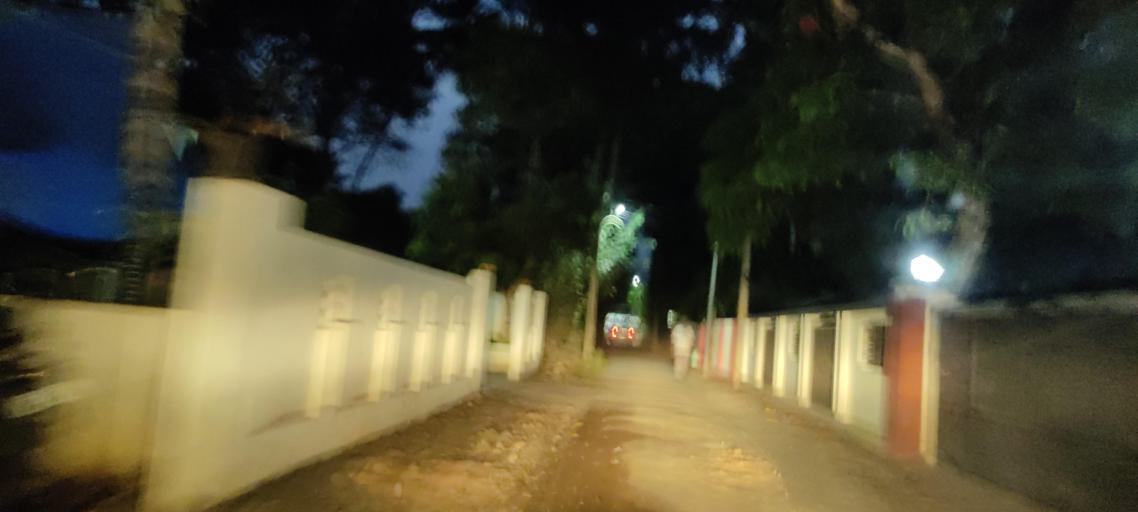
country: IN
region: Kerala
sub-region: Alappuzha
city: Mavelikara
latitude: 9.3195
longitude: 76.4267
